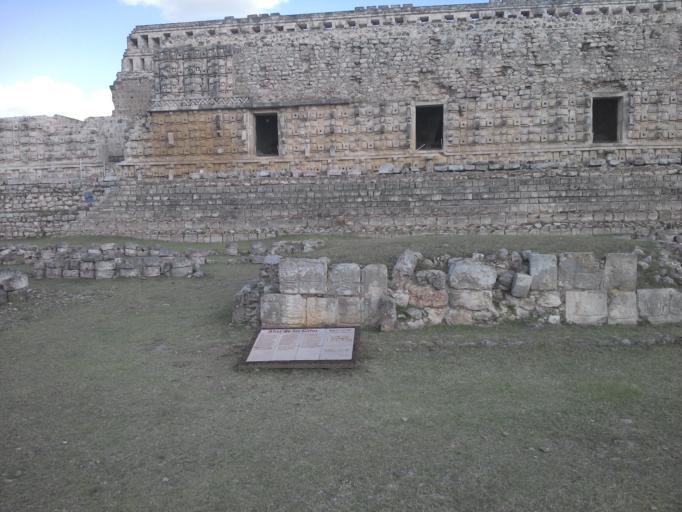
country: MX
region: Yucatan
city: Santa Elena
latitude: 20.2480
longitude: -89.6478
